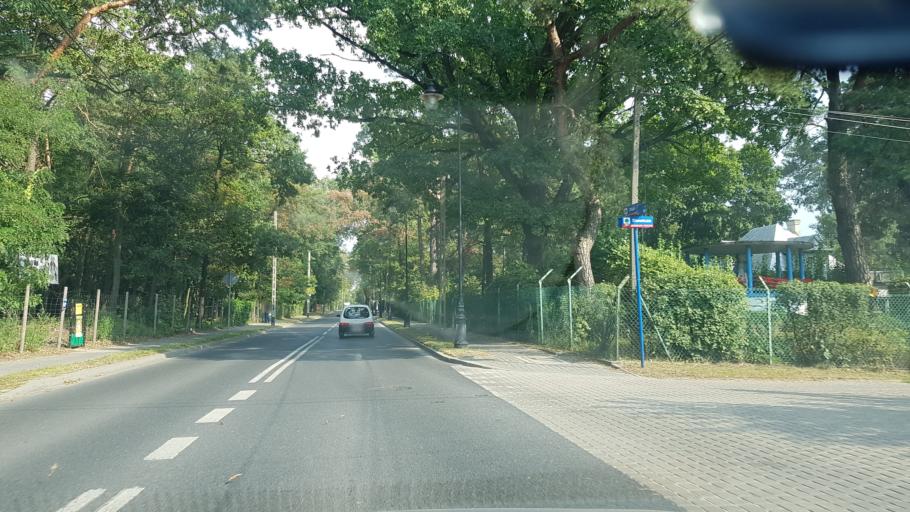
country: PL
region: Masovian Voivodeship
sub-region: Powiat piaseczynski
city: Konstancin-Jeziorna
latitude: 52.0781
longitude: 21.0894
